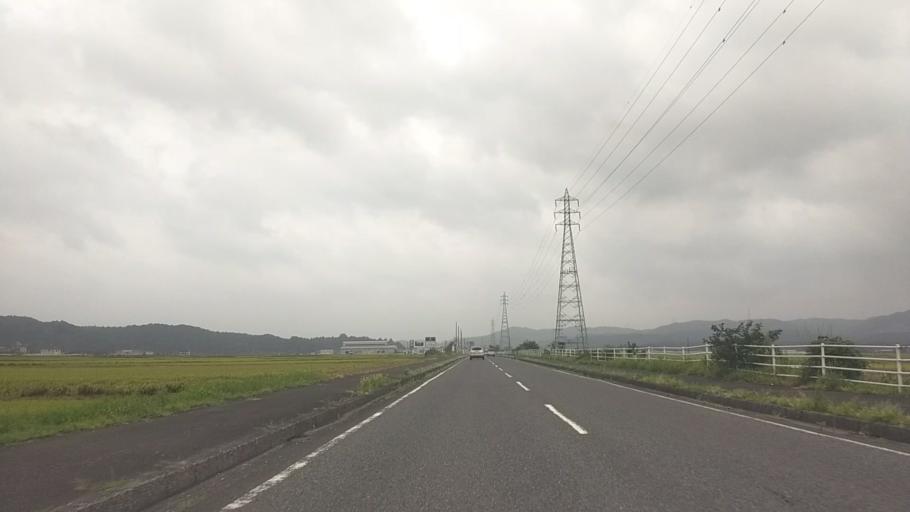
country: JP
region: Chiba
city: Kisarazu
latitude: 35.3354
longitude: 140.0549
